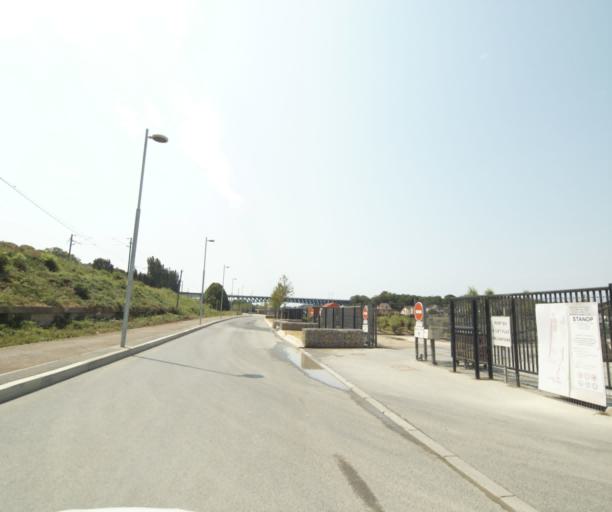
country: FR
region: Ile-de-France
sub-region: Departement des Yvelines
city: Maurecourt
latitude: 48.9952
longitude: 2.0729
